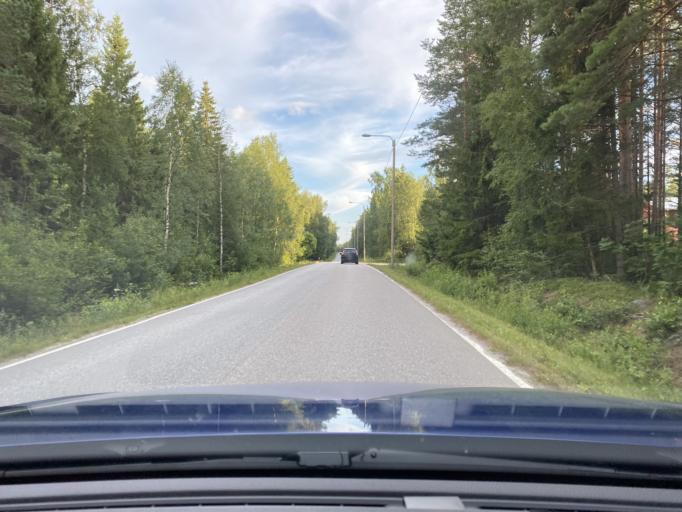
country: FI
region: Ostrobothnia
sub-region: Vaasa
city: Korsnaes
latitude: 62.9522
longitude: 21.1763
